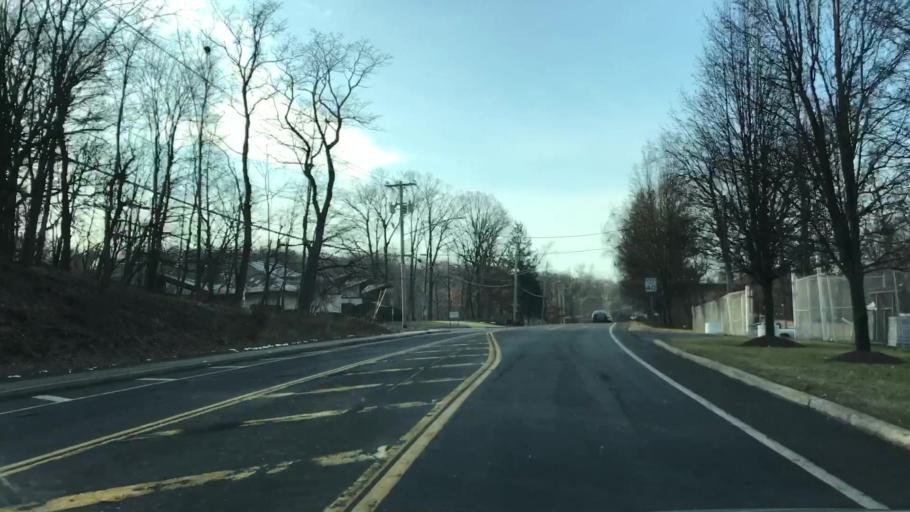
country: US
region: New York
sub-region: Rockland County
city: Valley Cottage
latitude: 41.1170
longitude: -73.9417
